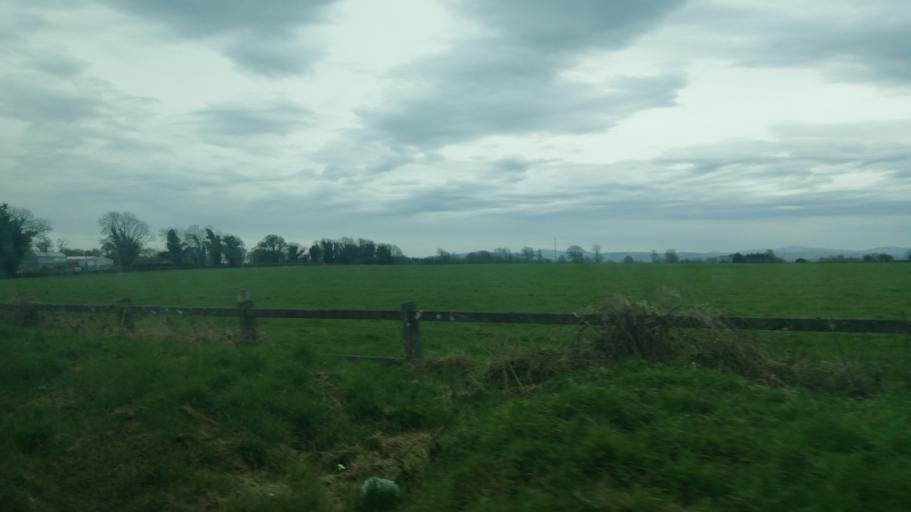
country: IE
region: Leinster
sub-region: Kildare
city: Clane
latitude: 53.3135
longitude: -6.6495
